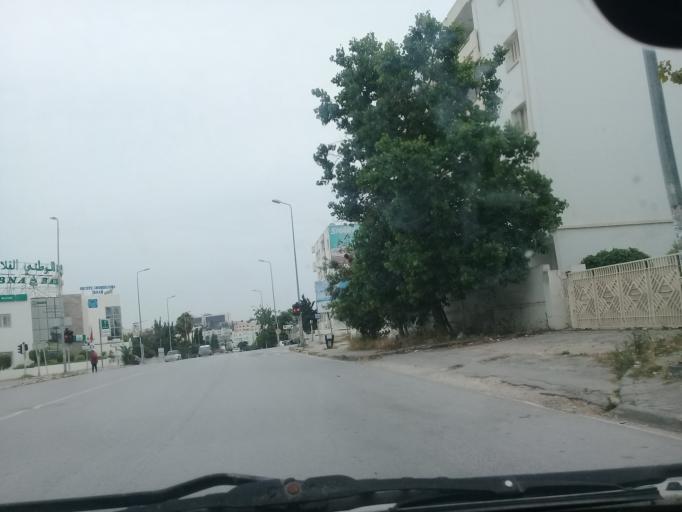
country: TN
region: Tunis
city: Tunis
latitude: 36.8437
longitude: 10.1543
